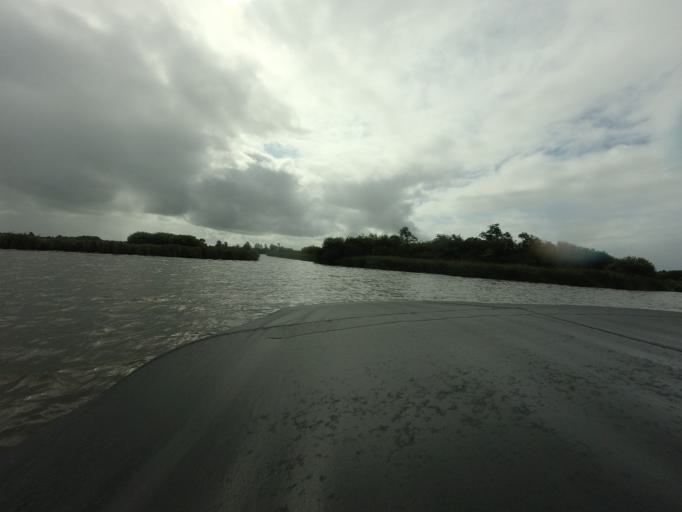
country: NL
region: Friesland
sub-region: Gemeente Boarnsterhim
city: Warten
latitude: 53.1323
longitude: 5.8963
